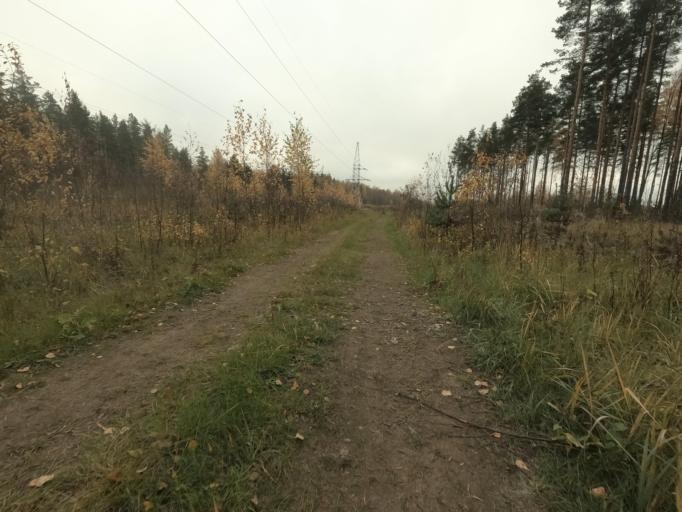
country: RU
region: Leningrad
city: Kirovsk
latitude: 59.8489
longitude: 30.9828
